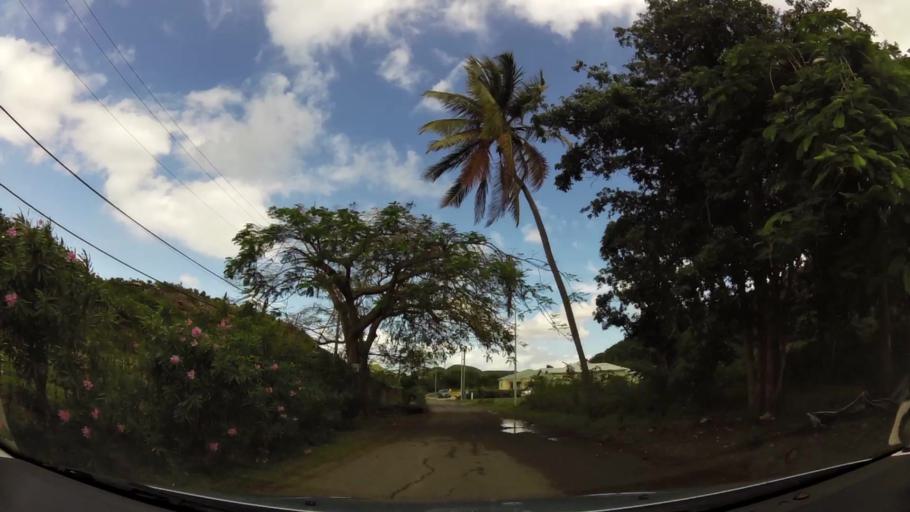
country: AG
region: Saint John
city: Saint John's
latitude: 17.1184
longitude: -61.8893
